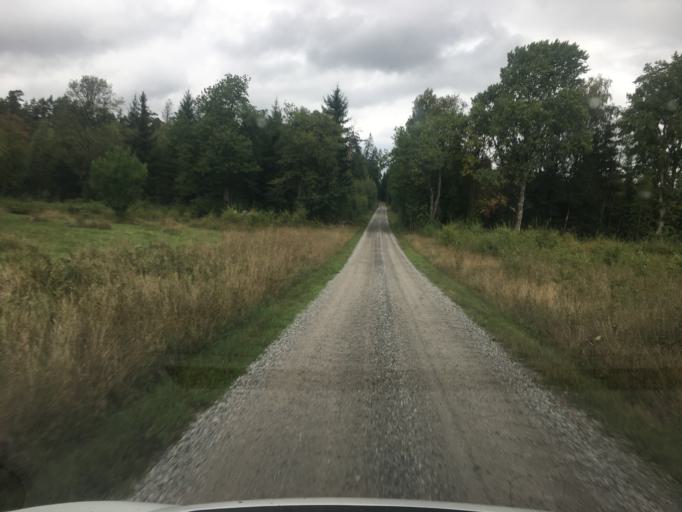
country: SE
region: Kronoberg
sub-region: Ljungby Kommun
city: Lagan
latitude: 56.9574
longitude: 14.0422
